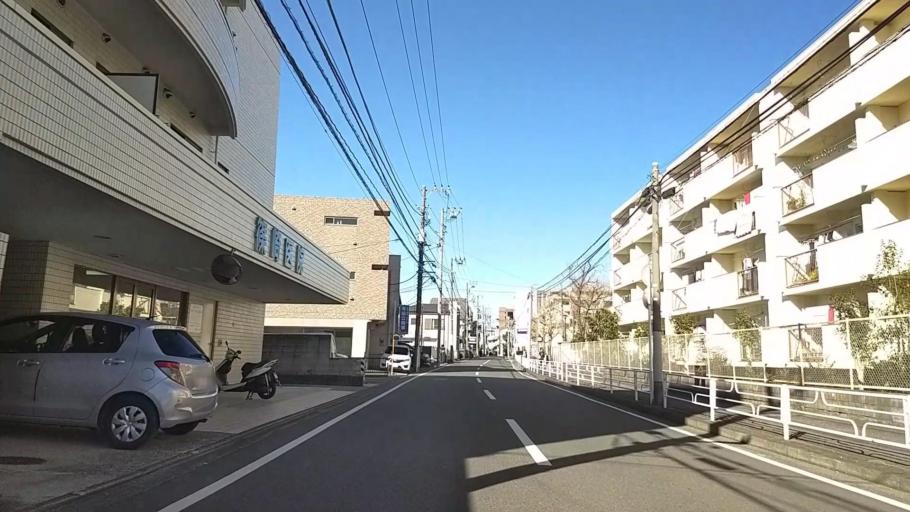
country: JP
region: Kanagawa
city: Yokohama
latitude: 35.4698
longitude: 139.5762
